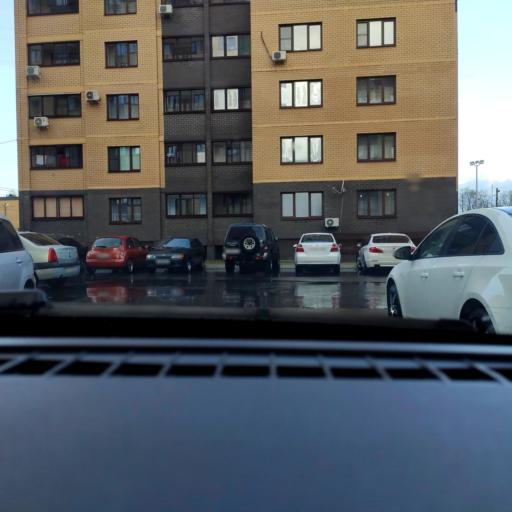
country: RU
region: Voronezj
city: Voronezh
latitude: 51.6660
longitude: 39.2802
